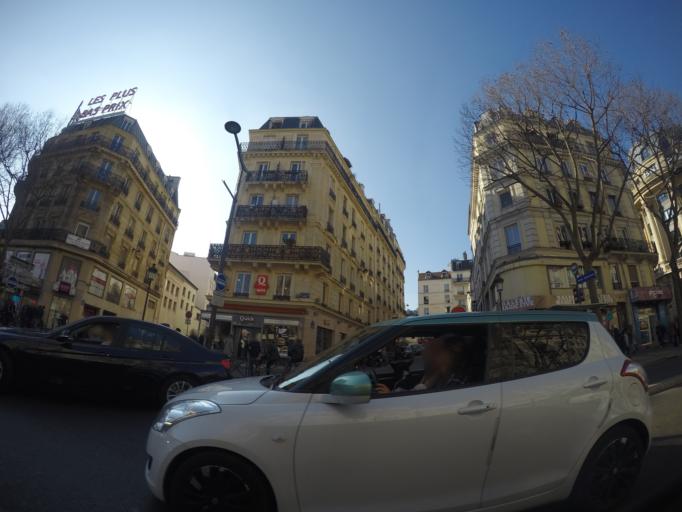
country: FR
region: Ile-de-France
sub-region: Paris
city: Saint-Ouen
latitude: 48.8839
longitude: 2.3488
